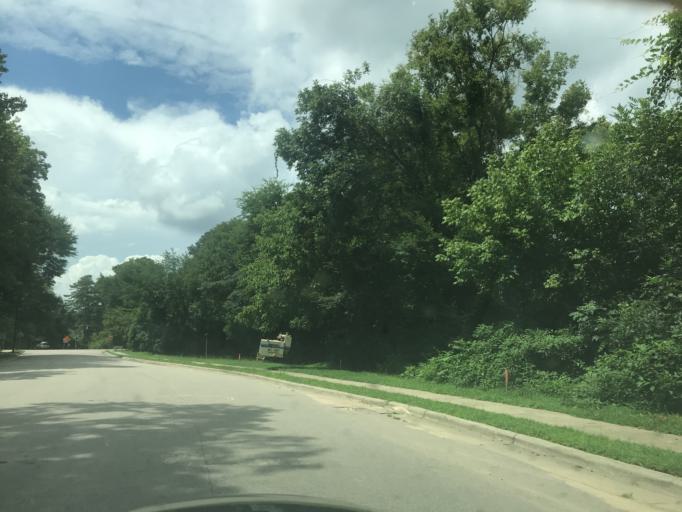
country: US
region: North Carolina
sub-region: Wake County
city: West Raleigh
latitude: 35.8200
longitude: -78.6335
